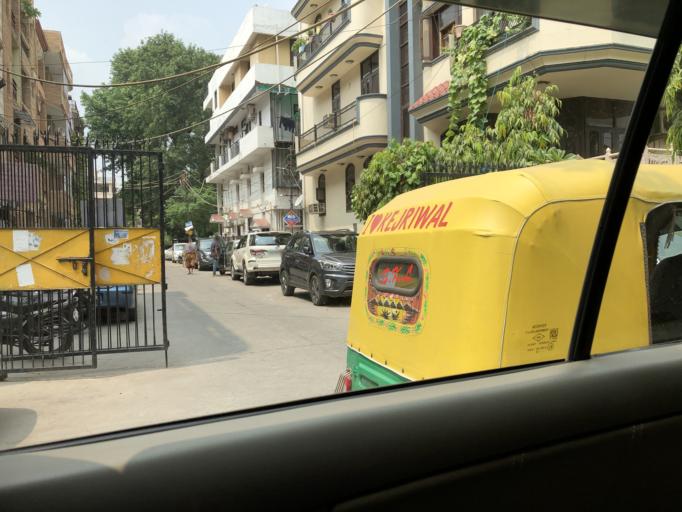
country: IN
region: NCT
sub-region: New Delhi
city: New Delhi
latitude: 28.5733
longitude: 77.2433
